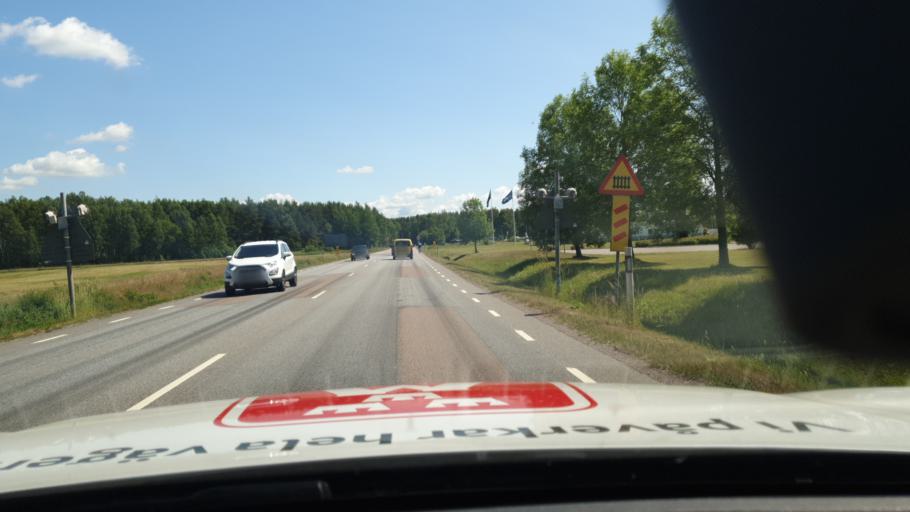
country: SE
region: Vaestra Goetaland
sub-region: Lidkopings Kommun
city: Lidkoping
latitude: 58.5013
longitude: 13.1273
